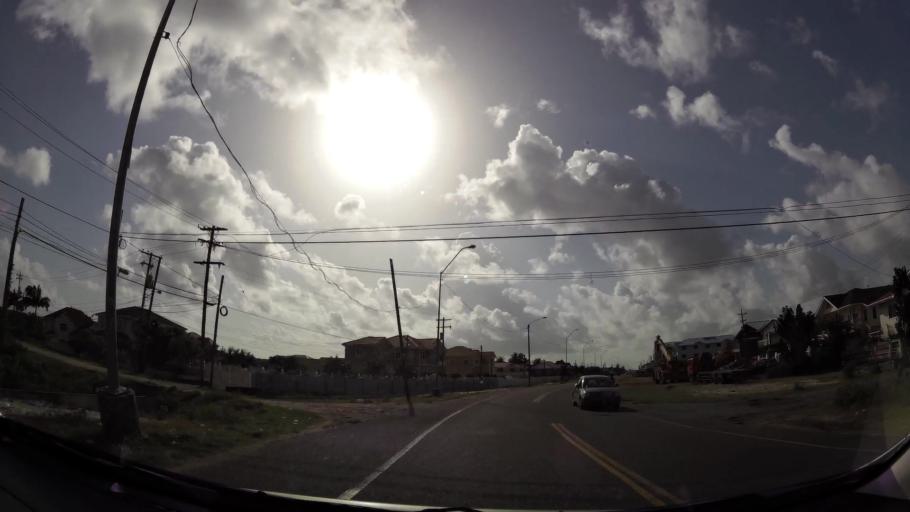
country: GY
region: Demerara-Mahaica
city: Georgetown
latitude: 6.8177
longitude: -58.0778
